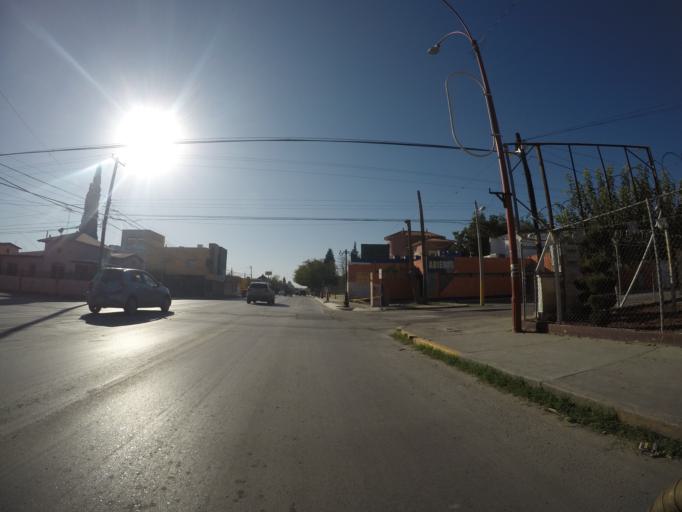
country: MX
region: Chihuahua
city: Ciudad Juarez
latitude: 31.7383
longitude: -106.4684
